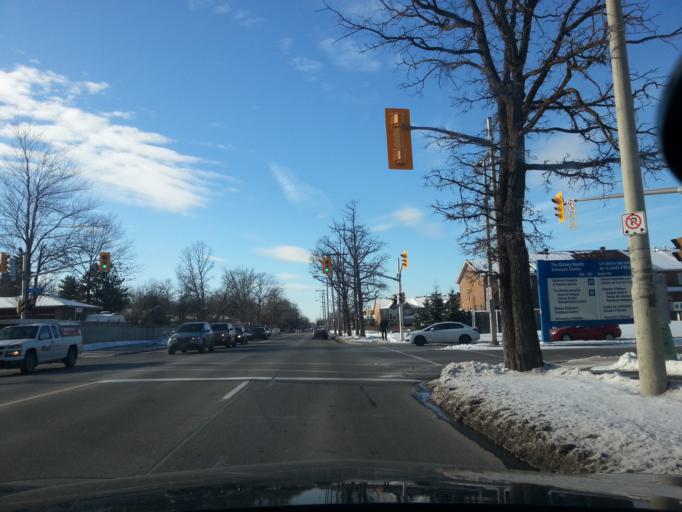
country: CA
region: Ontario
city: Ottawa
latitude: 45.3991
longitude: -75.6525
